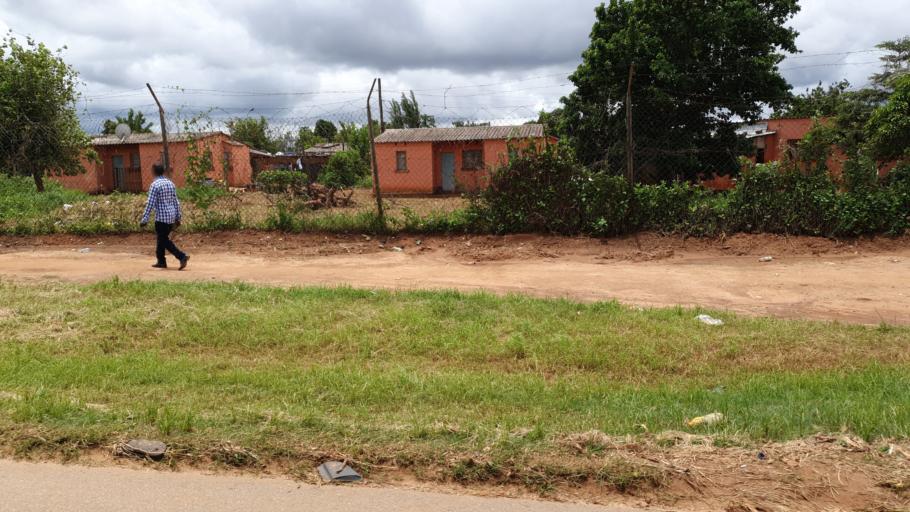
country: ZM
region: Lusaka
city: Lusaka
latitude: -15.4323
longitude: 28.3068
